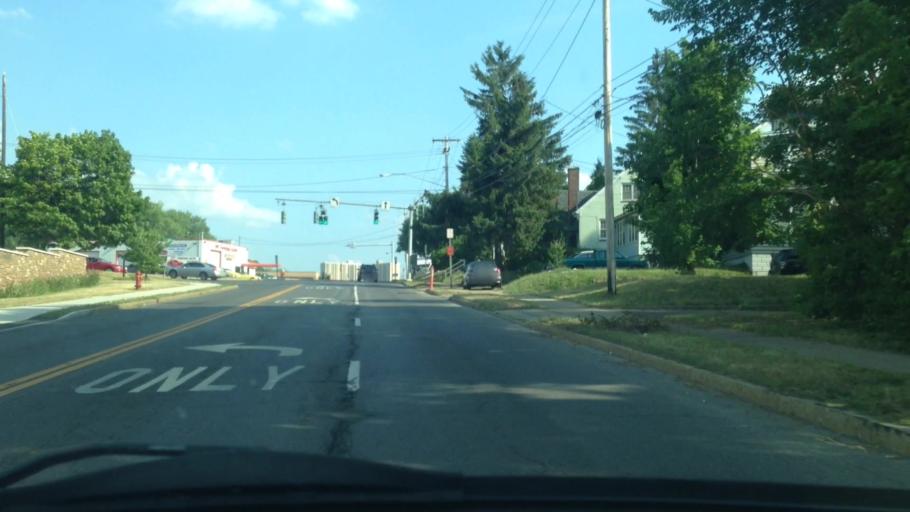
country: US
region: New York
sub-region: Onondaga County
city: Syracuse
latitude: 43.0183
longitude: -76.1383
